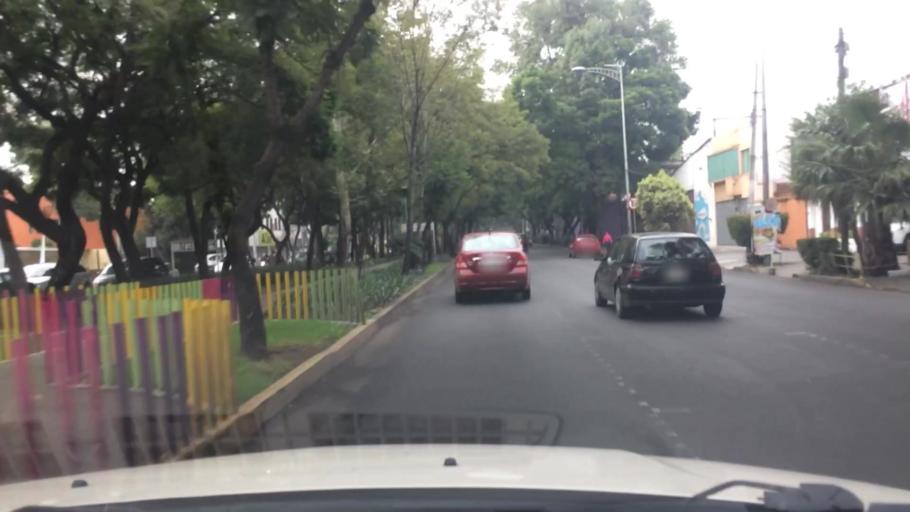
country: MX
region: Mexico City
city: Coyoacan
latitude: 19.3251
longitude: -99.1360
